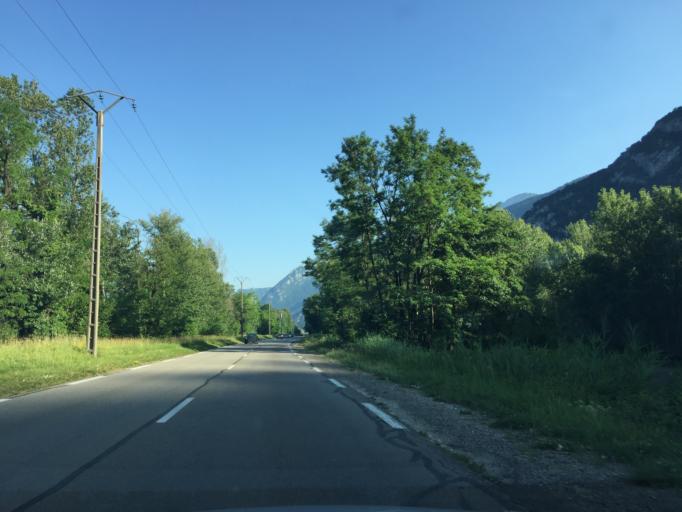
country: FR
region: Rhone-Alpes
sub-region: Departement de l'Isere
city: Voreppe
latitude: 45.2917
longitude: 5.6153
